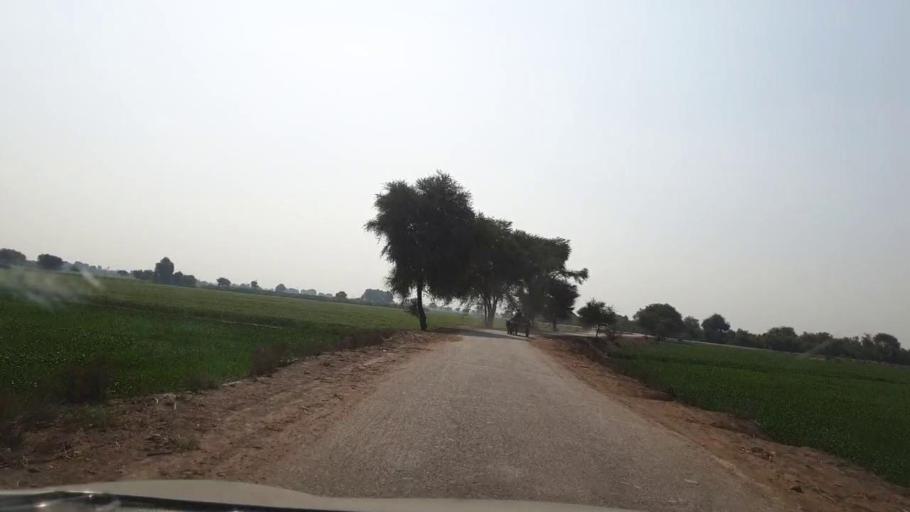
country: PK
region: Sindh
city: Bhit Shah
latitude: 25.7488
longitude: 68.4955
